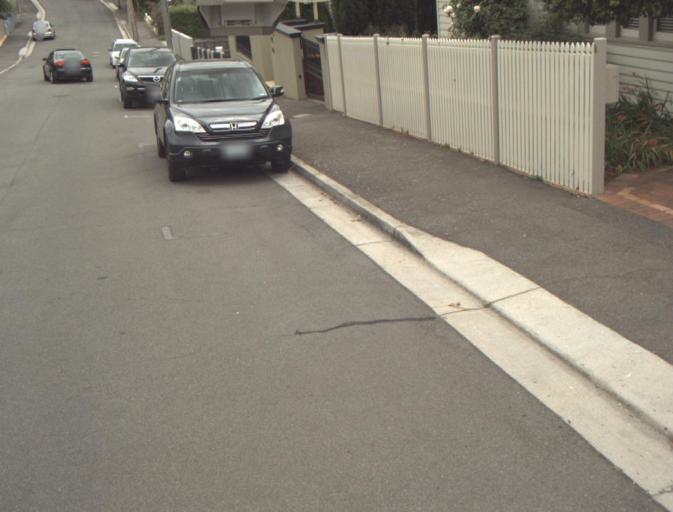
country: AU
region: Tasmania
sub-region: Launceston
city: East Launceston
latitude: -41.4426
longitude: 147.1505
